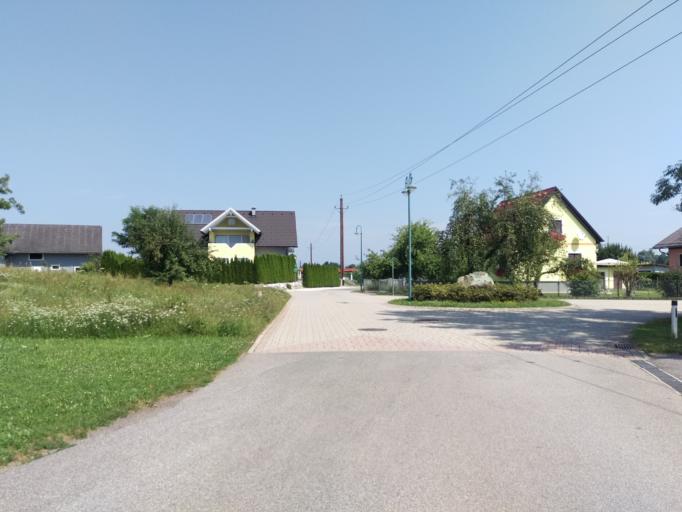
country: AT
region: Styria
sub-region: Politischer Bezirk Graz-Umgebung
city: Kalsdorf bei Graz
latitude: 46.9461
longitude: 15.4884
